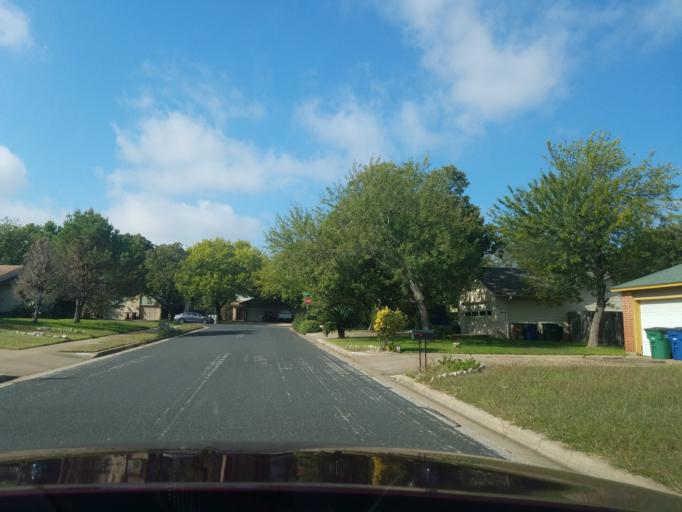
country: US
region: Texas
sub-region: Williamson County
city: Jollyville
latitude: 30.4495
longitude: -97.7801
